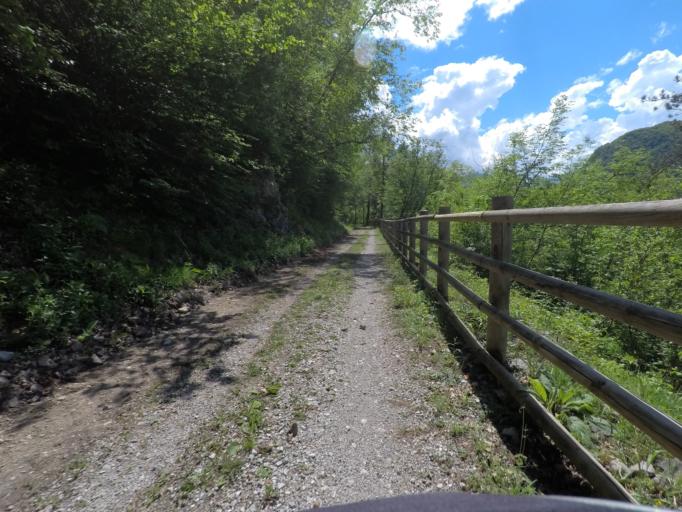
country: IT
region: Friuli Venezia Giulia
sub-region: Provincia di Udine
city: Raveo
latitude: 46.4571
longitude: 12.8751
